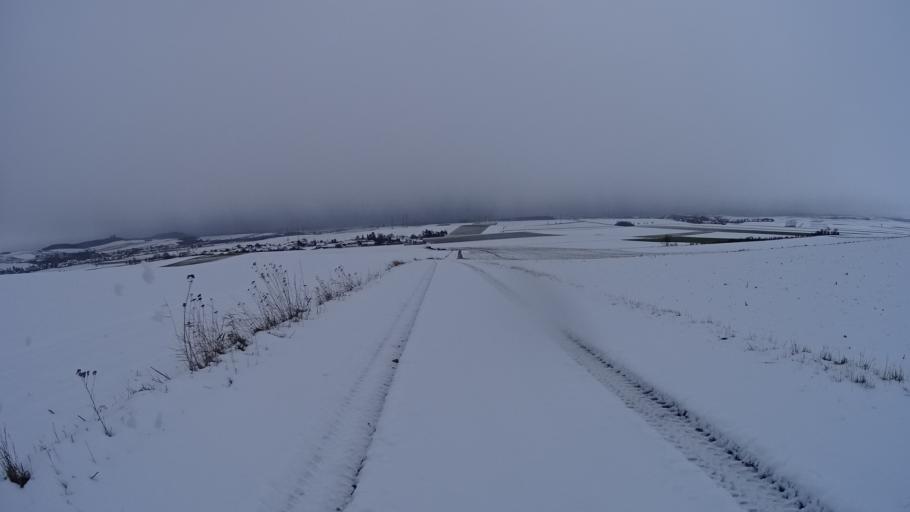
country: AT
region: Lower Austria
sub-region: Politischer Bezirk Korneuburg
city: Niederhollabrunn
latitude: 48.4130
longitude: 16.2810
